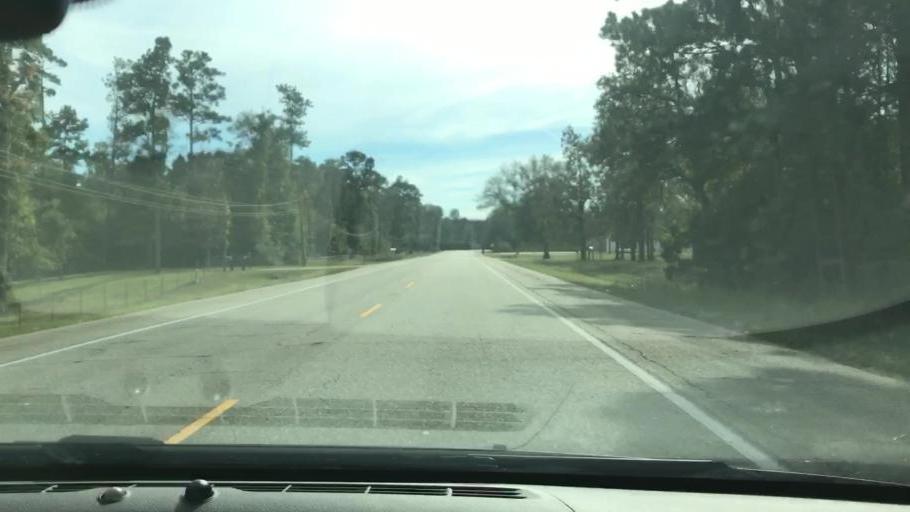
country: US
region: Mississippi
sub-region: Pearl River County
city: Nicholson
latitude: 30.5040
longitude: -89.8168
